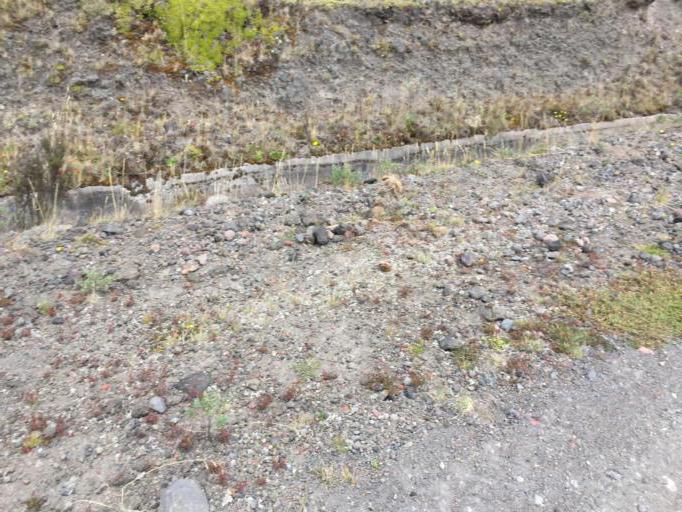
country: EC
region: Pichincha
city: Machachi
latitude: -0.6120
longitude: -78.4370
